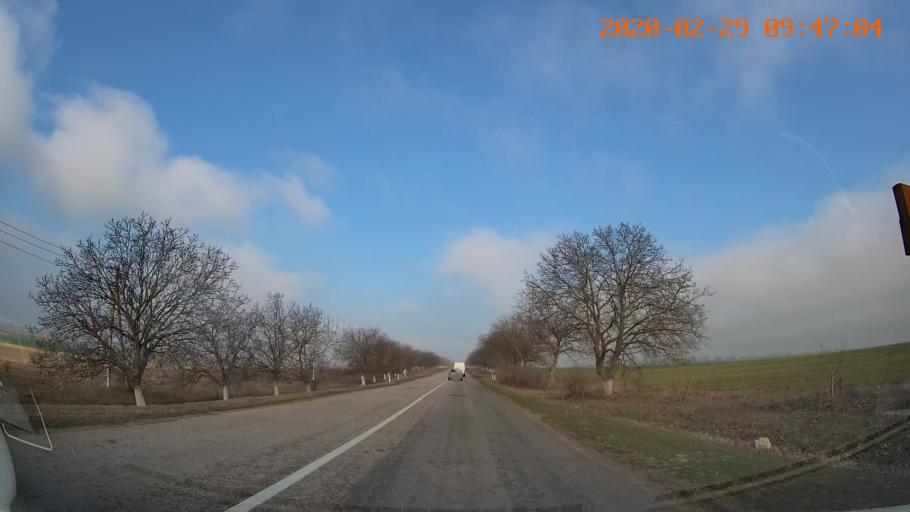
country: MD
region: Telenesti
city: Crasnoe
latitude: 46.6738
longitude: 29.7935
